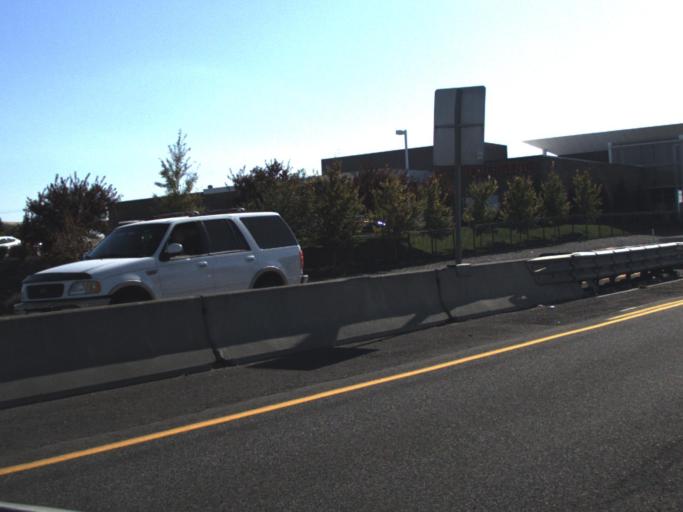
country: US
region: Washington
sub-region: Benton County
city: Kennewick
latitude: 46.1934
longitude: -119.1651
